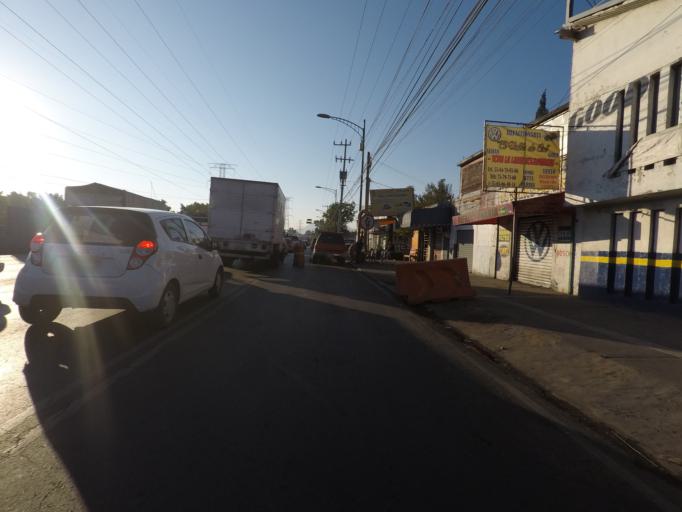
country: MX
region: Mexico City
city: Iztapalapa
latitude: 19.3668
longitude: -99.0723
